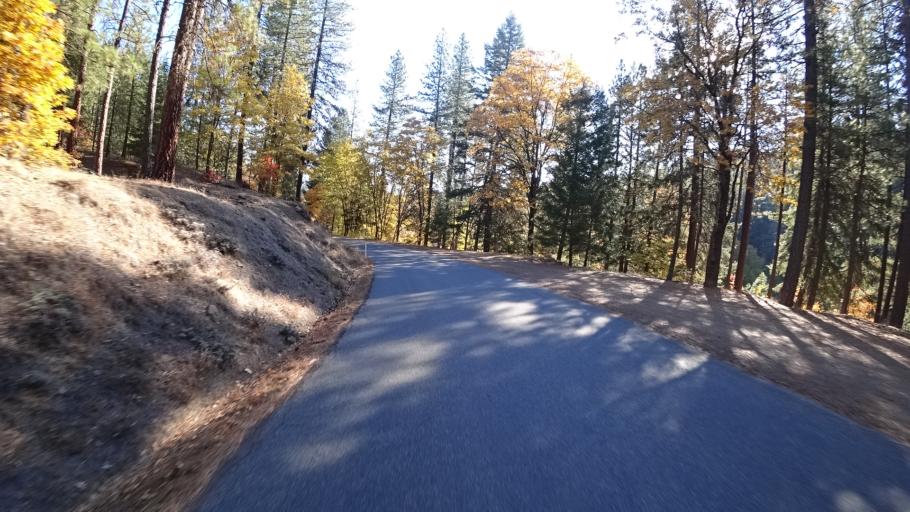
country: US
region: California
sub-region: Siskiyou County
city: Yreka
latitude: 41.6406
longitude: -123.0039
